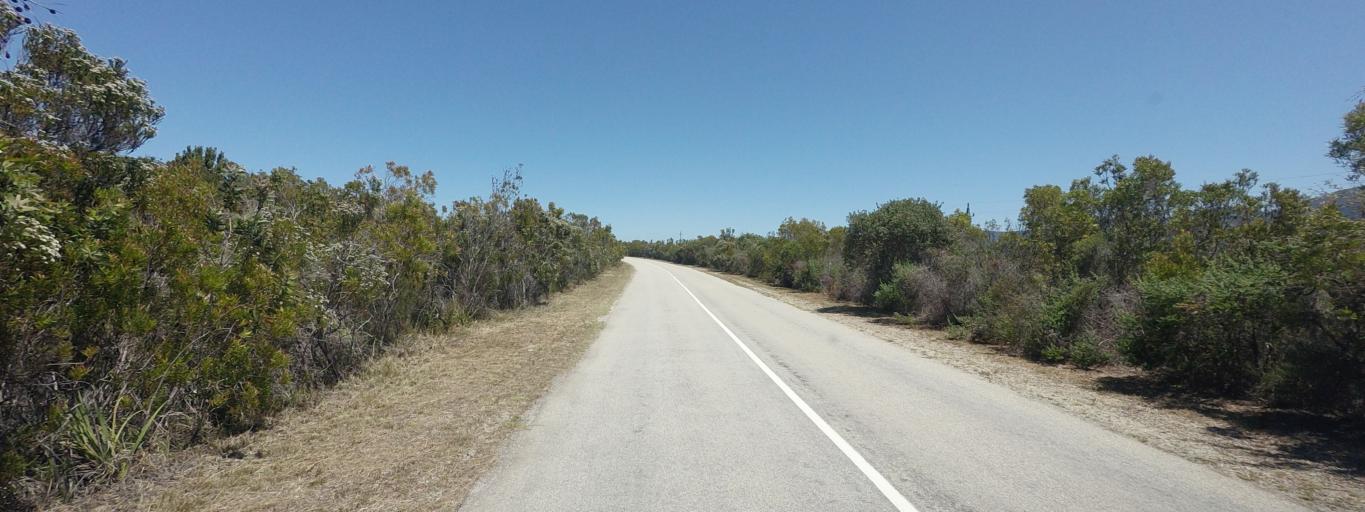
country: ZA
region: Western Cape
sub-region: Eden District Municipality
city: Plettenberg Bay
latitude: -33.9602
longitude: 23.5375
